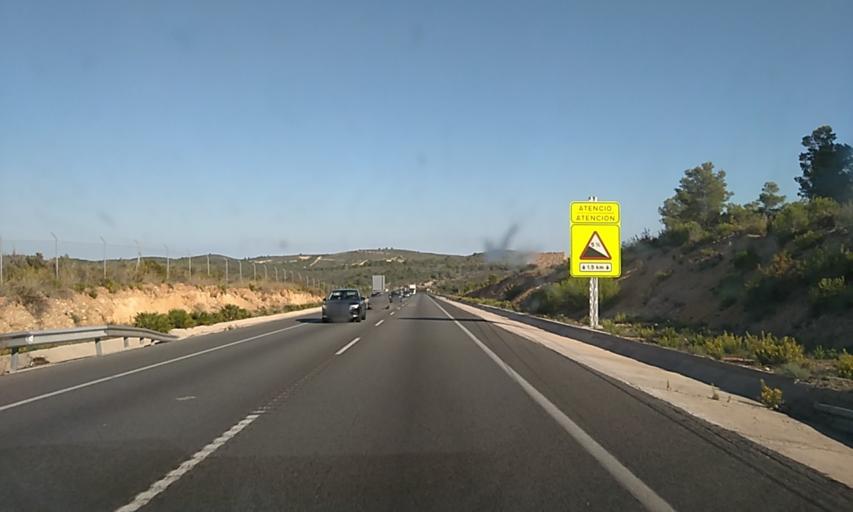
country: ES
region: Valencia
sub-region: Provincia de Castello
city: Torreblanca
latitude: 40.2108
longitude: 0.1306
